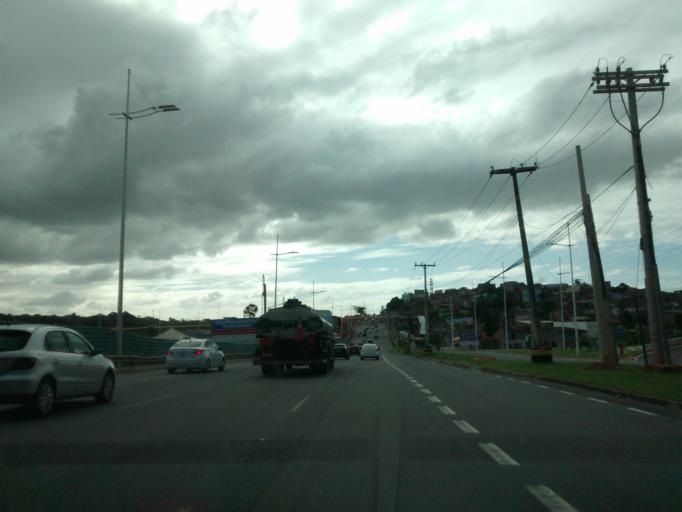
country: BR
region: Bahia
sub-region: Lauro De Freitas
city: Lauro de Freitas
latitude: -12.9262
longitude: -38.3820
